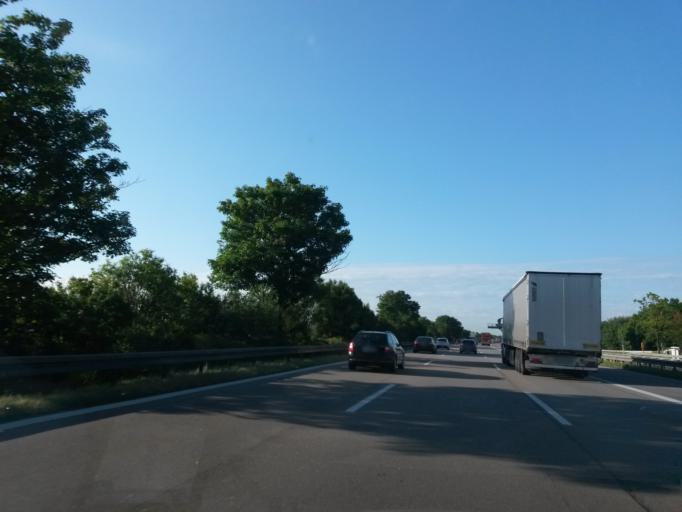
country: DE
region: Bavaria
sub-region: Upper Bavaria
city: Feldkirchen
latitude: 48.1426
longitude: 11.7576
